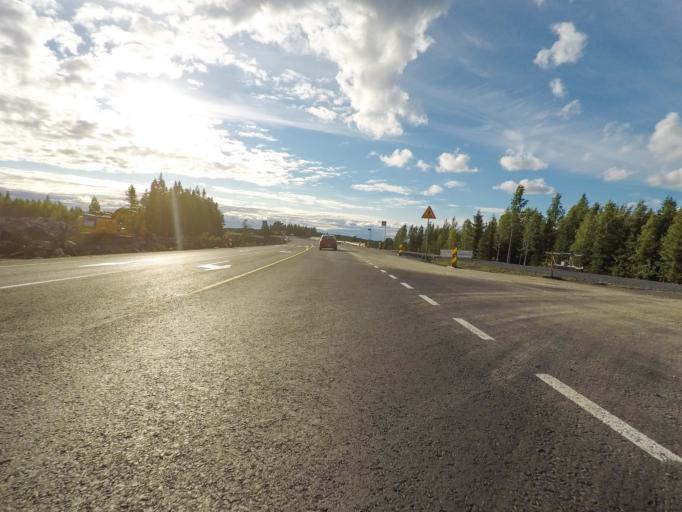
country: FI
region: Northern Savo
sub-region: Kuopio
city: Kuopio
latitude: 62.9679
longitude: 27.8451
